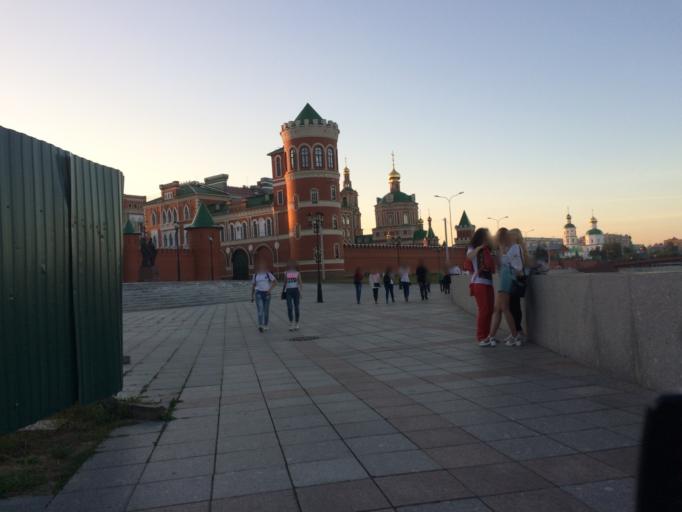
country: RU
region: Mariy-El
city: Yoshkar-Ola
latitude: 56.6353
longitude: 47.9042
